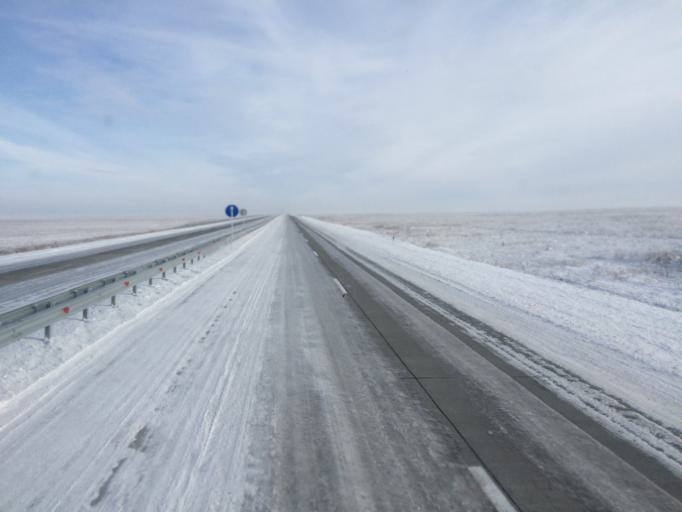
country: KZ
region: Zhambyl
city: Georgiyevka
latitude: 43.3480
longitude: 74.5137
